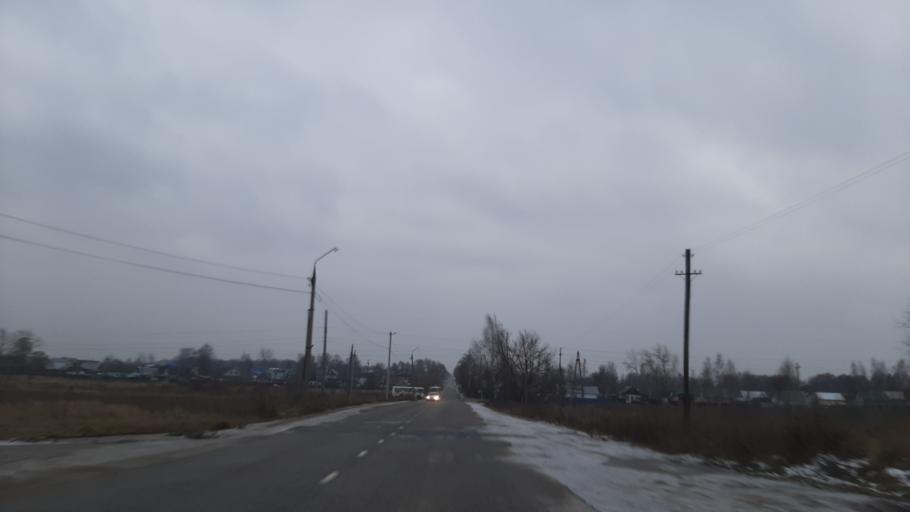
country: RU
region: Ivanovo
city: Shuya
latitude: 56.8785
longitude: 41.3463
